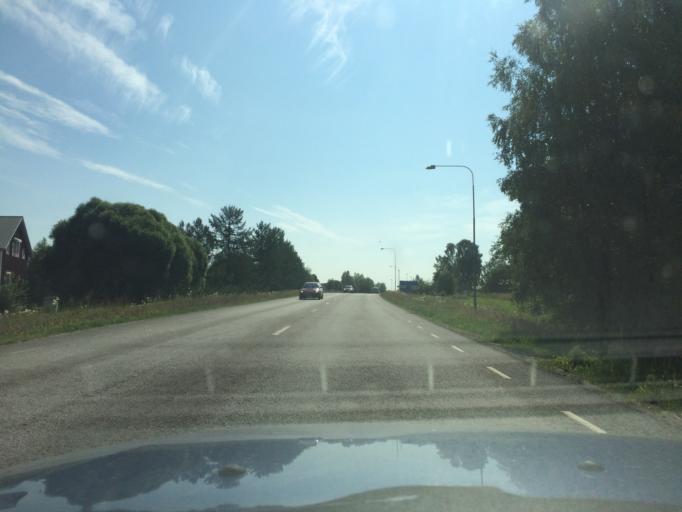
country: SE
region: Norrbotten
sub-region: Pitea Kommun
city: Bergsviken
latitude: 65.3487
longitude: 21.4040
